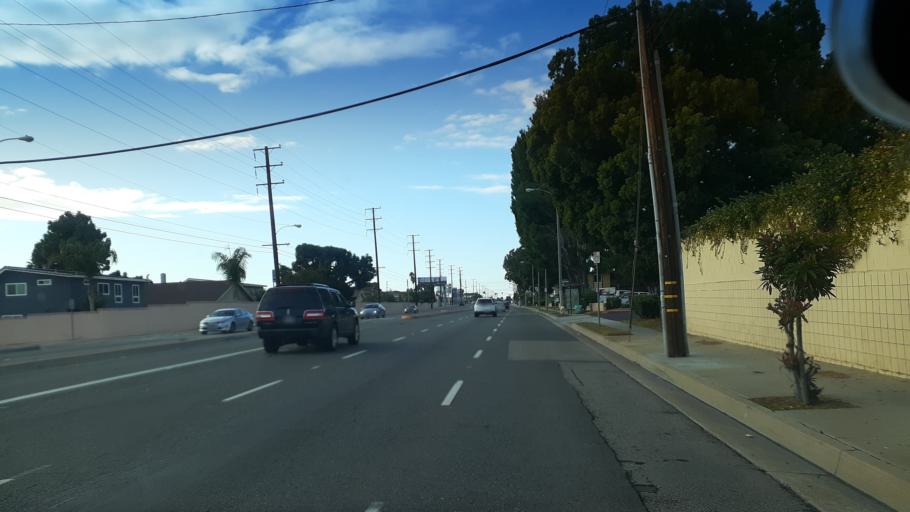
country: US
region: California
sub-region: Los Angeles County
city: West Carson
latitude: 33.8116
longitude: -118.2937
